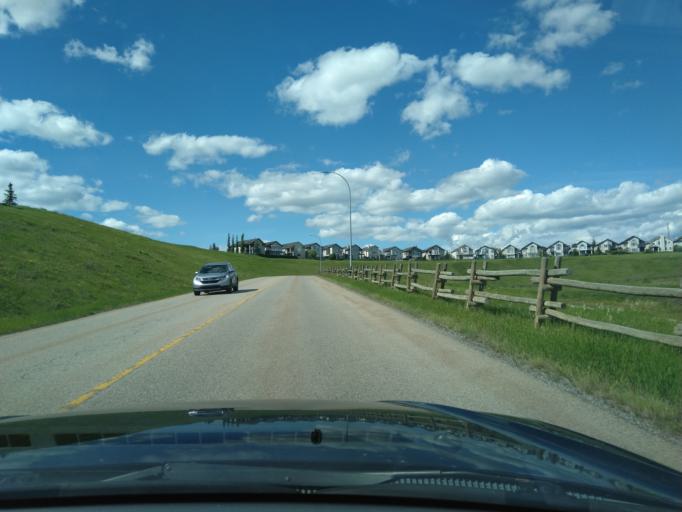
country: CA
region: Alberta
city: Cochrane
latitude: 51.1928
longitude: -114.4269
